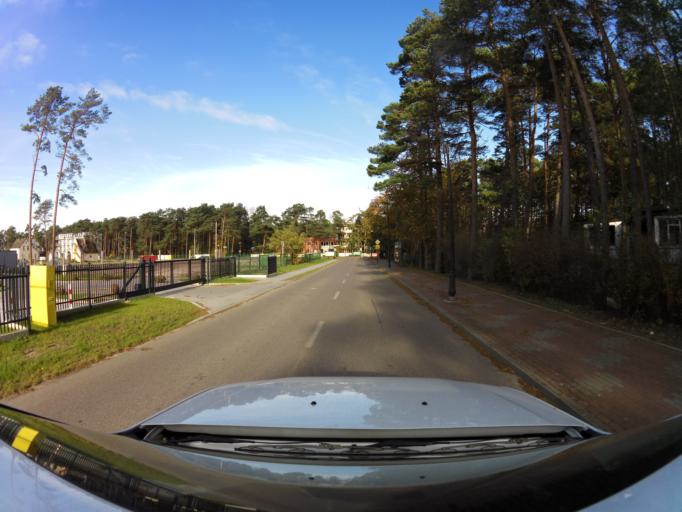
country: PL
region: West Pomeranian Voivodeship
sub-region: Powiat gryficki
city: Cerkwica
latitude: 54.1020
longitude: 15.1210
